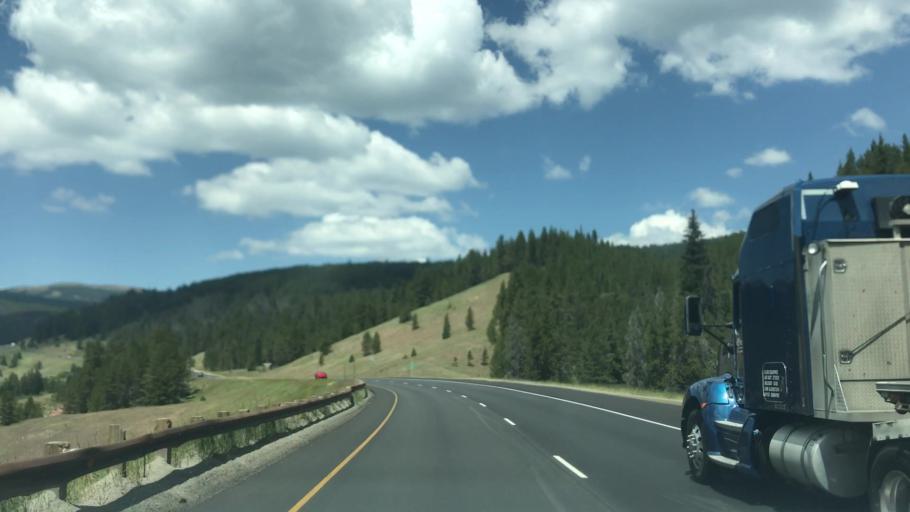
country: US
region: Colorado
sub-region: Summit County
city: Frisco
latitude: 39.5054
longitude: -106.1807
